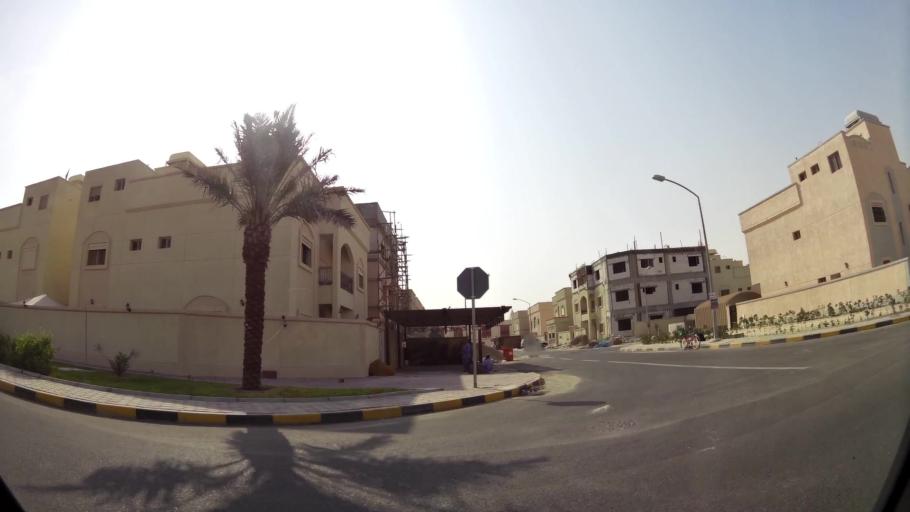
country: KW
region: Muhafazat al Jahra'
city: Al Jahra'
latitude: 29.3561
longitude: 47.7518
